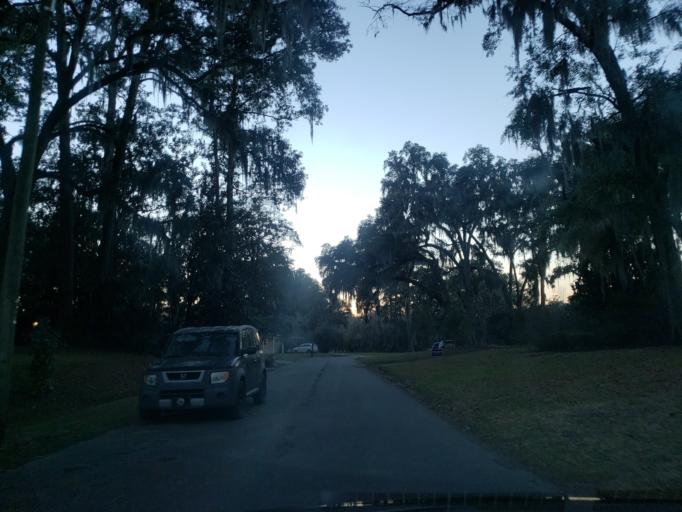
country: US
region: Georgia
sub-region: Chatham County
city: Thunderbolt
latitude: 32.0202
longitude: -81.0856
